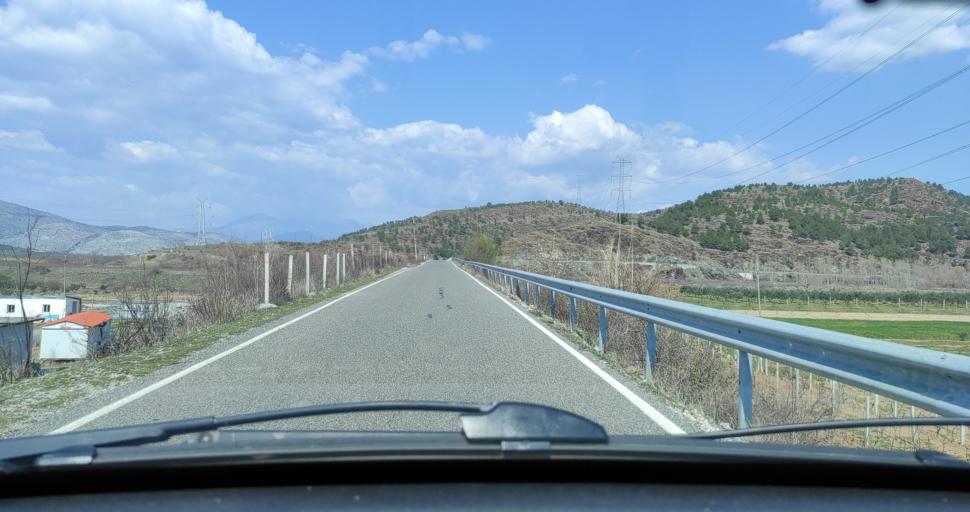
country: AL
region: Shkoder
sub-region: Rrethi i Shkodres
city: Hajmel
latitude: 41.9756
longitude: 19.6449
